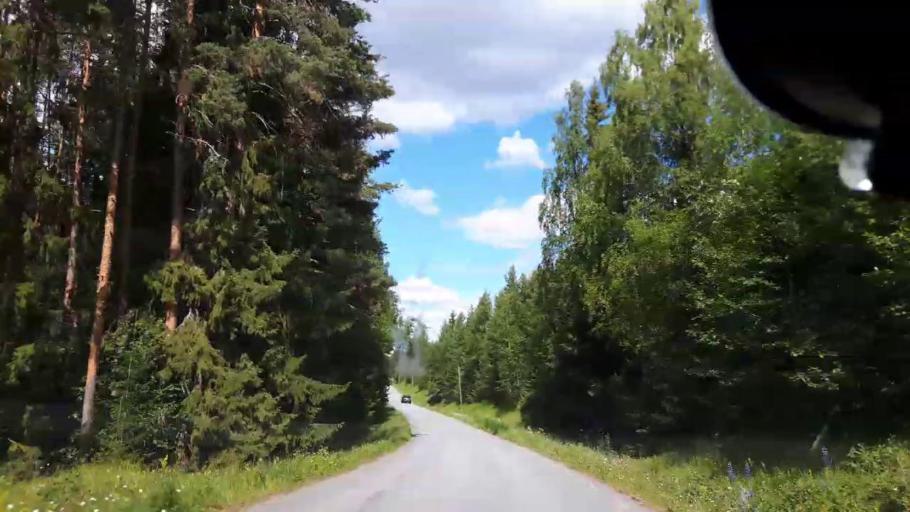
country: SE
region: Jaemtland
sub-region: Ragunda Kommun
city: Hammarstrand
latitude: 62.9349
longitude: 16.6930
